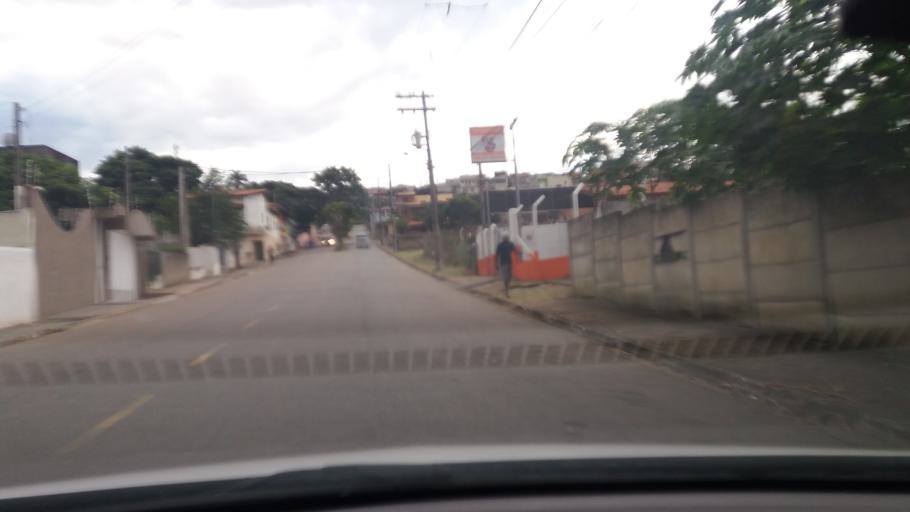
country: BR
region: Sao Paulo
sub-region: Bom Jesus Dos Perdoes
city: Bom Jesus dos Perdoes
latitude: -23.1259
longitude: -46.4710
